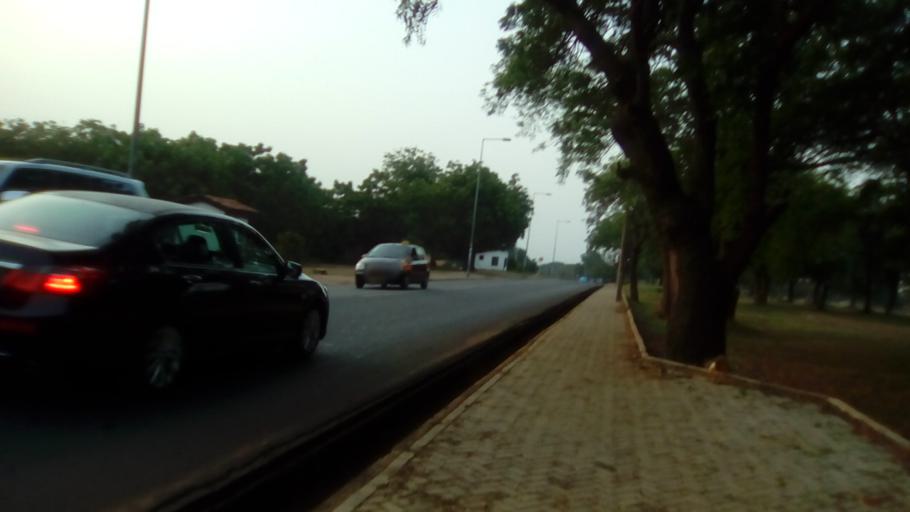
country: GH
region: Greater Accra
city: Medina Estates
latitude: 5.6417
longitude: -0.1842
